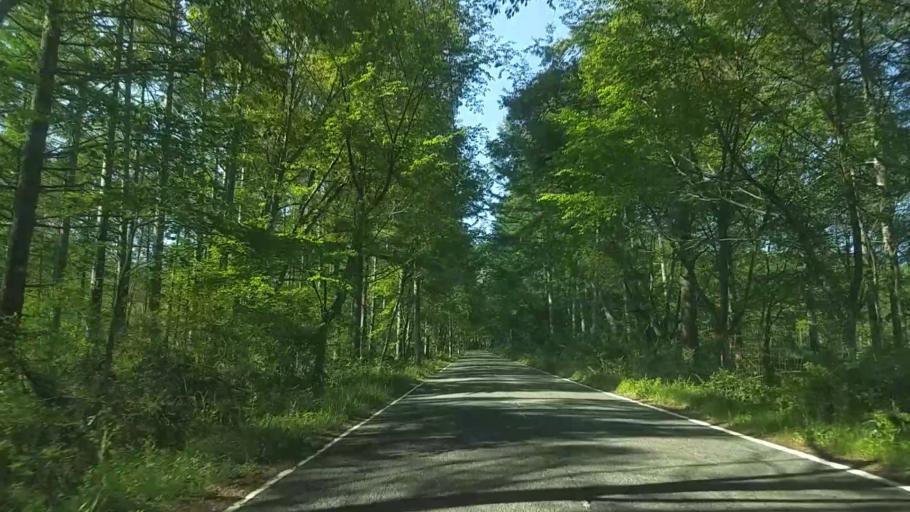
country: JP
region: Nagano
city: Chino
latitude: 35.8971
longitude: 138.3504
